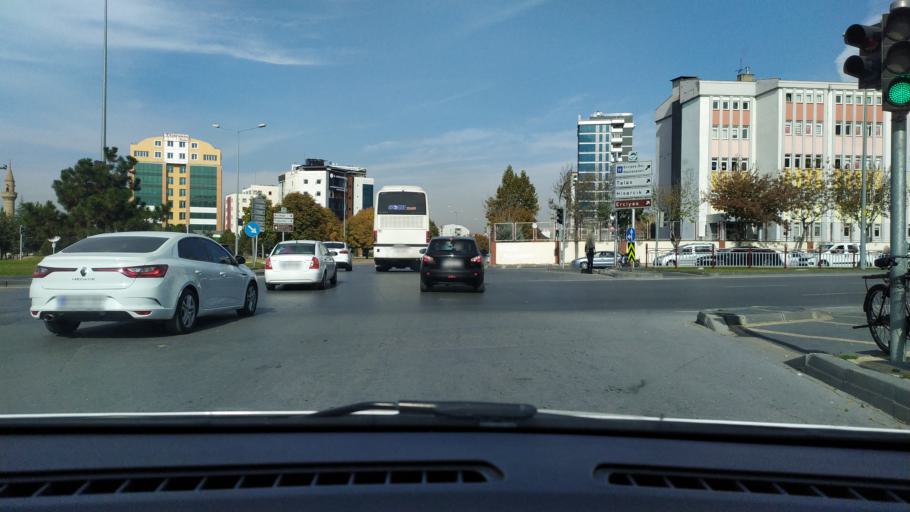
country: TR
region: Kayseri
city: Kayseri
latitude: 38.7107
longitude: 35.4912
